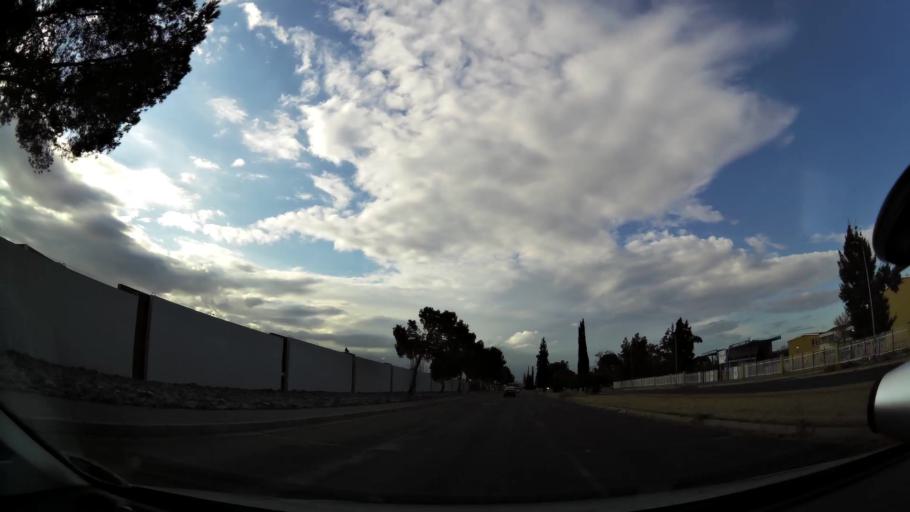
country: ZA
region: Orange Free State
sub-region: Lejweleputswa District Municipality
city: Welkom
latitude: -27.9898
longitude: 26.7337
